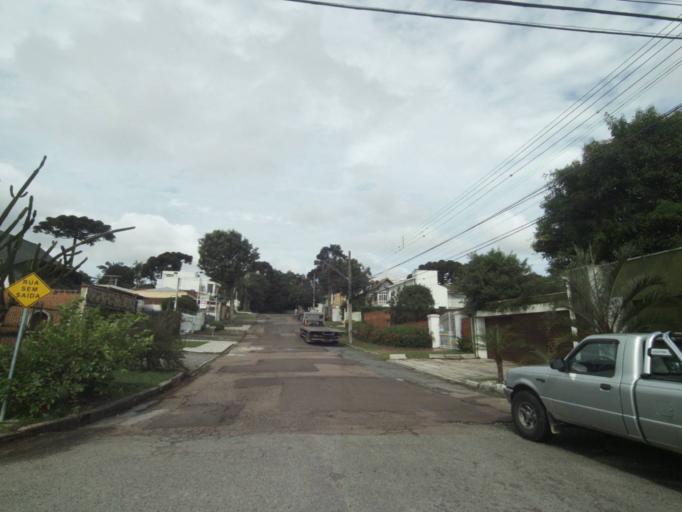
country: BR
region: Parana
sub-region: Curitiba
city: Curitiba
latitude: -25.4448
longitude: -49.3031
